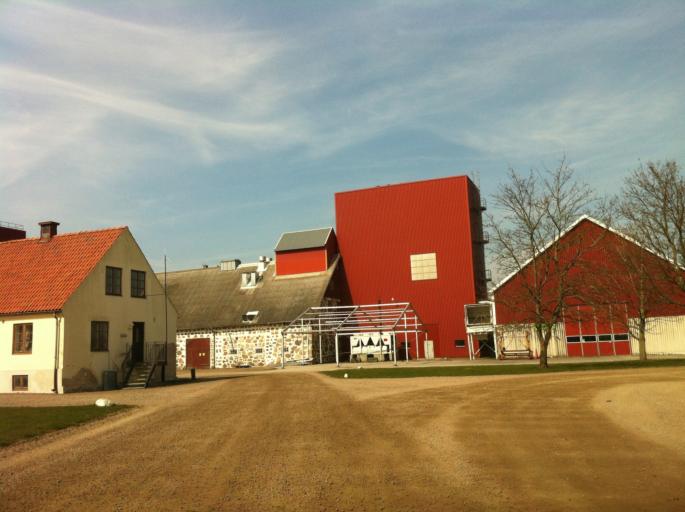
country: SE
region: Skane
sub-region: Svalovs Kommun
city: Svaloev
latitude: 55.9264
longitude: 13.1005
